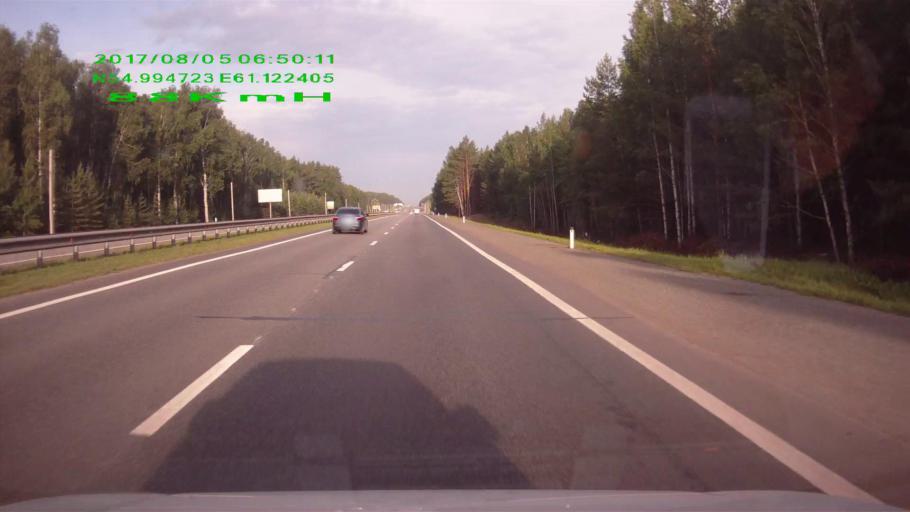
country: RU
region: Chelyabinsk
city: Poletayevo
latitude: 54.9947
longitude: 61.1221
